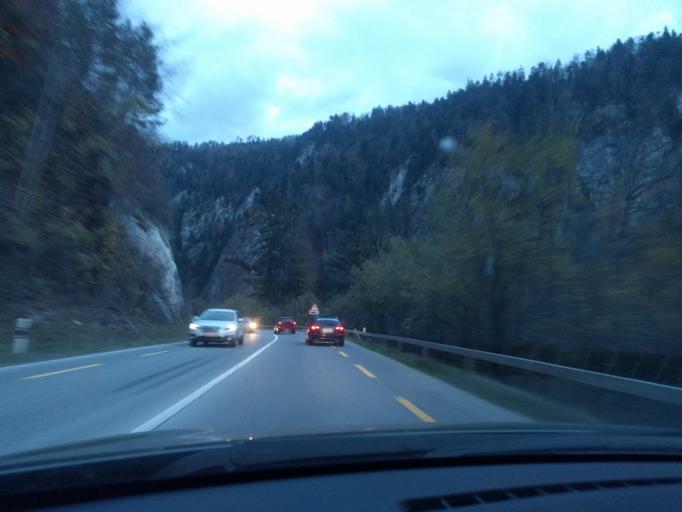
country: CH
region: Bern
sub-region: Frutigen-Niedersimmental District
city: Wimmis
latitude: 46.6706
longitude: 7.6130
